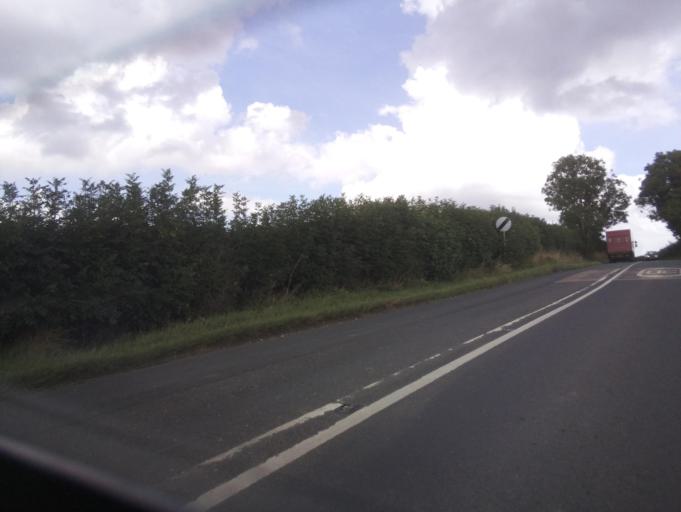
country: GB
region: England
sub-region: North Yorkshire
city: Catterick Garrison
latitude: 54.4218
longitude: -1.6868
